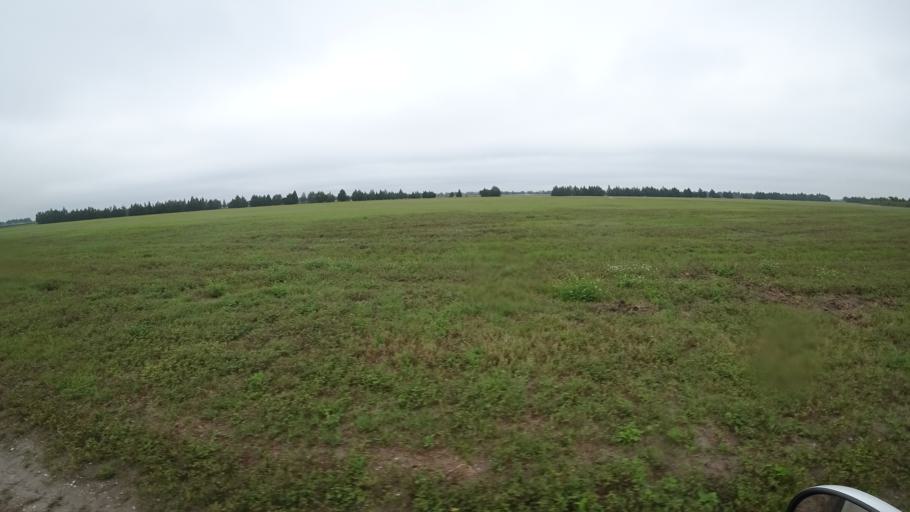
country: US
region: Florida
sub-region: Sarasota County
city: Warm Mineral Springs
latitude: 27.3040
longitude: -82.1475
